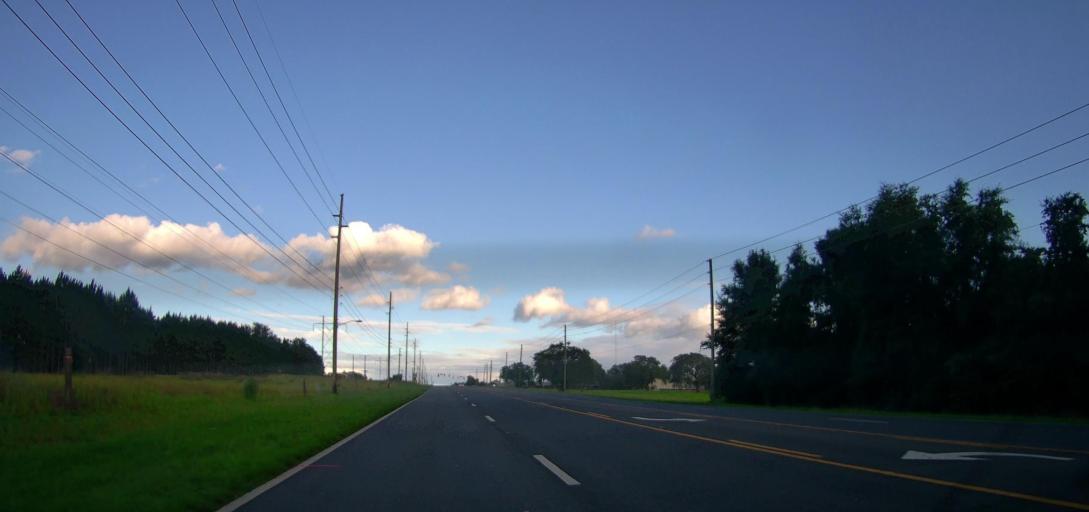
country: US
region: Florida
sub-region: Marion County
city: Silver Springs Shores
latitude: 29.0921
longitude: -81.9997
